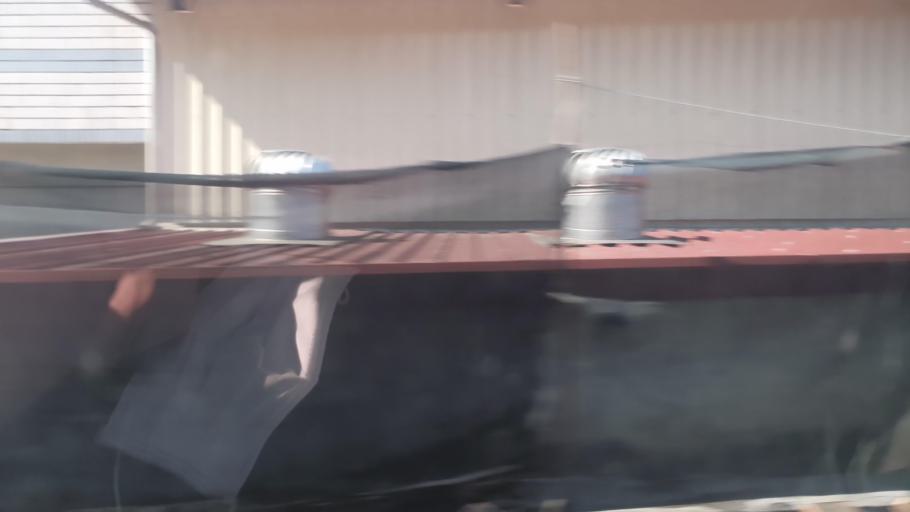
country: TW
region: Taiwan
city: Yujing
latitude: 23.0630
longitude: 120.3814
